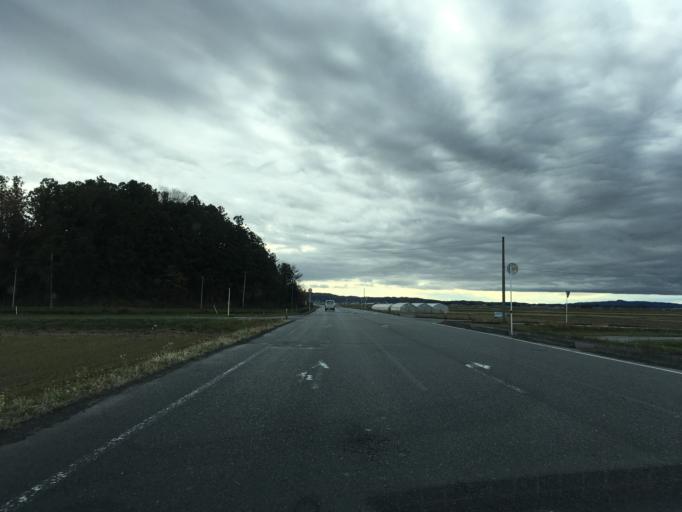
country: JP
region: Miyagi
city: Wakuya
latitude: 38.6964
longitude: 141.2604
